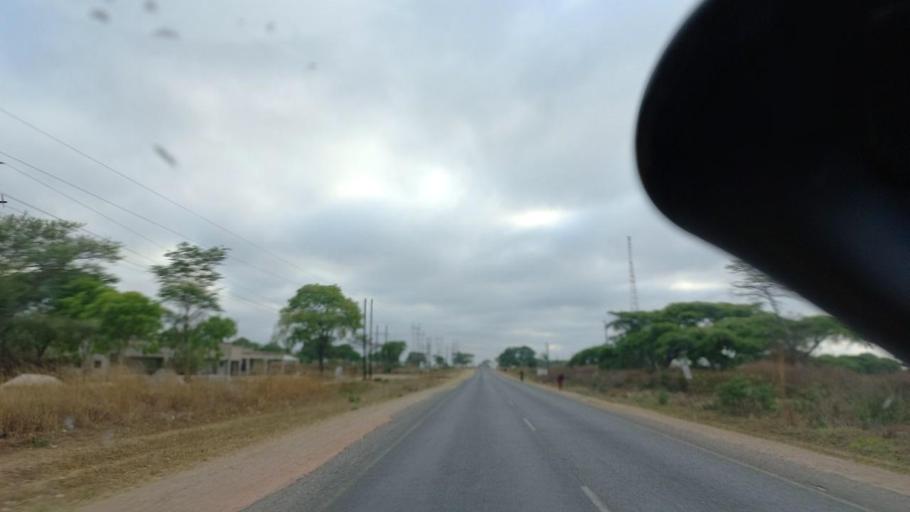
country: ZM
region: Lusaka
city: Chongwe
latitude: -15.3445
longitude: 28.5122
